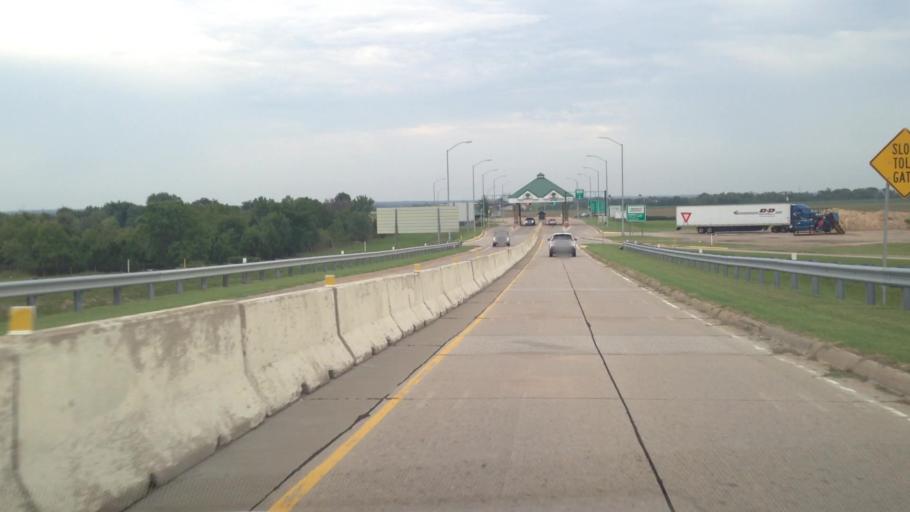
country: US
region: Oklahoma
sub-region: Ottawa County
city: Afton
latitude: 36.7218
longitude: -94.9352
